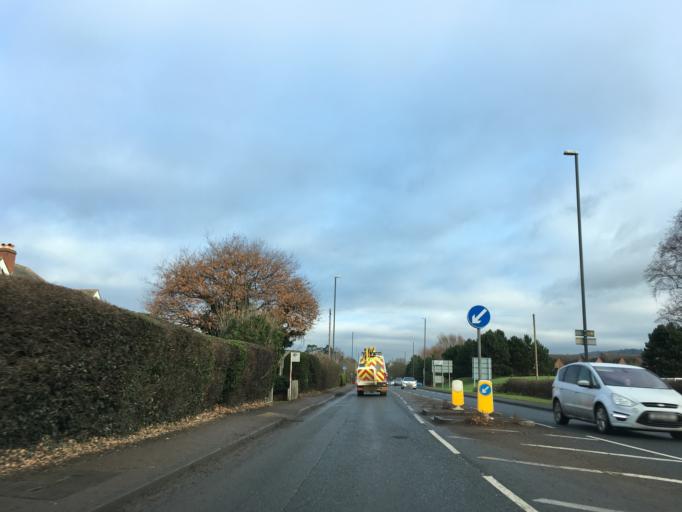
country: GB
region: England
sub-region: Gloucestershire
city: Shurdington
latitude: 51.8430
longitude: -2.1484
